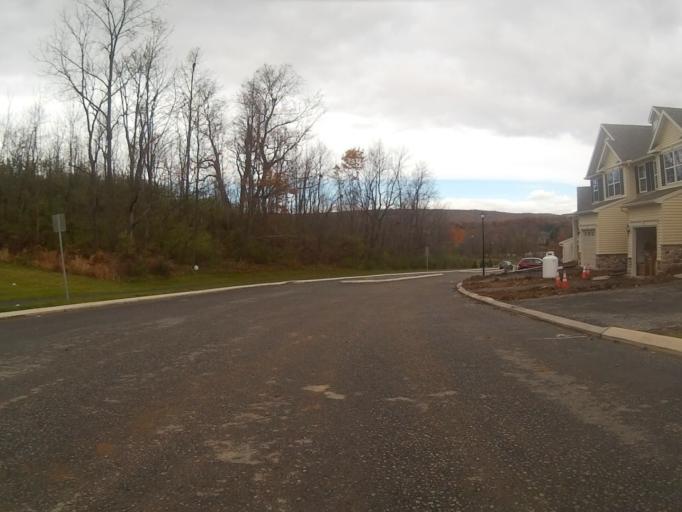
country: US
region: Pennsylvania
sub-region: Centre County
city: Boalsburg
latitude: 40.7758
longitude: -77.7779
